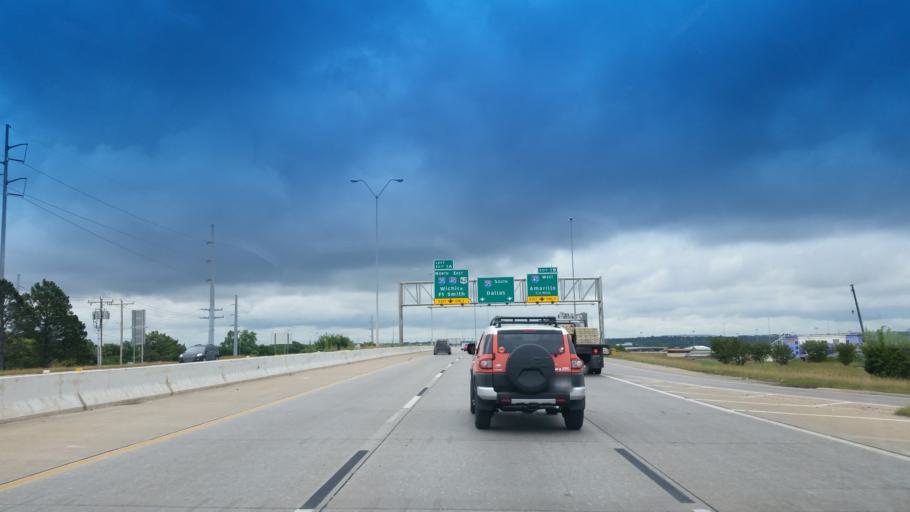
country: US
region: Oklahoma
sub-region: Oklahoma County
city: Oklahoma City
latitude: 35.4710
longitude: -97.5047
